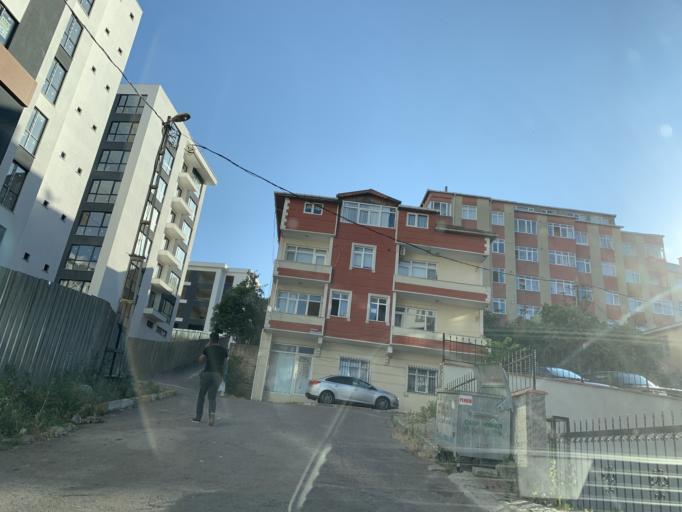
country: TR
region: Istanbul
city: Pendik
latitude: 40.8918
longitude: 29.2561
